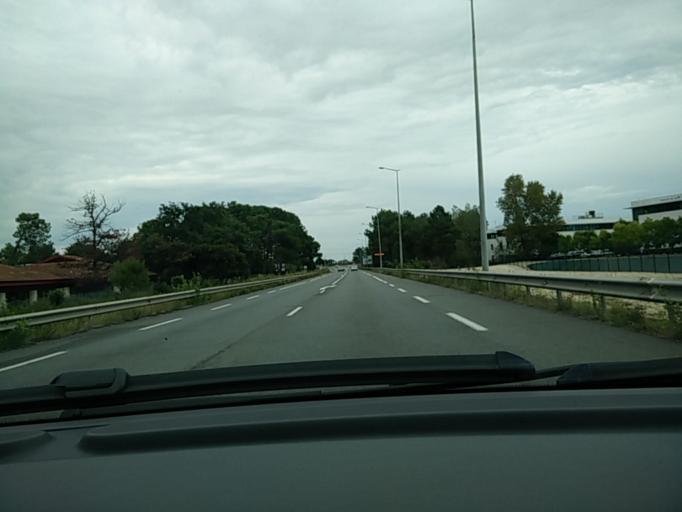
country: FR
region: Aquitaine
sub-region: Departement de la Gironde
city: Le Haillan
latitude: 44.8331
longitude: -0.6853
